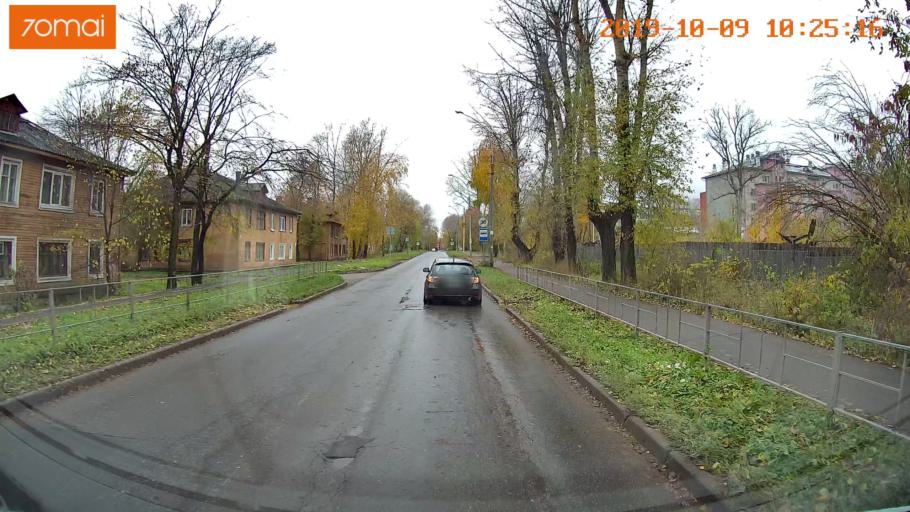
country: RU
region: Vologda
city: Vologda
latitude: 59.2129
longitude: 39.9333
